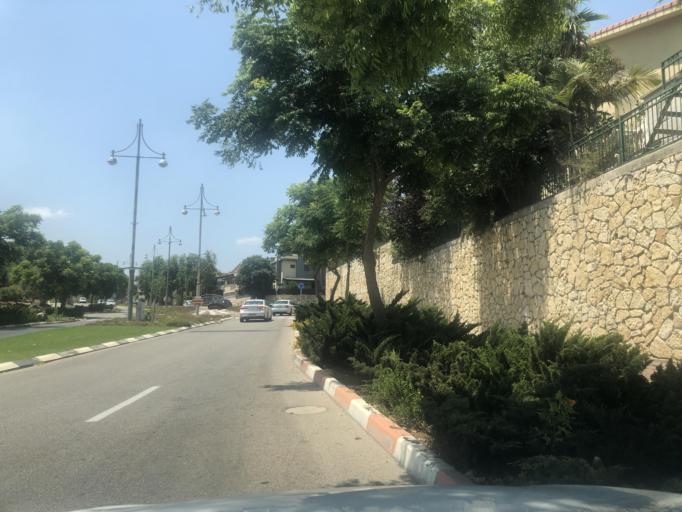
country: IL
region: Haifa
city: Daliyat el Karmil
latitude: 32.6394
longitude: 35.0857
